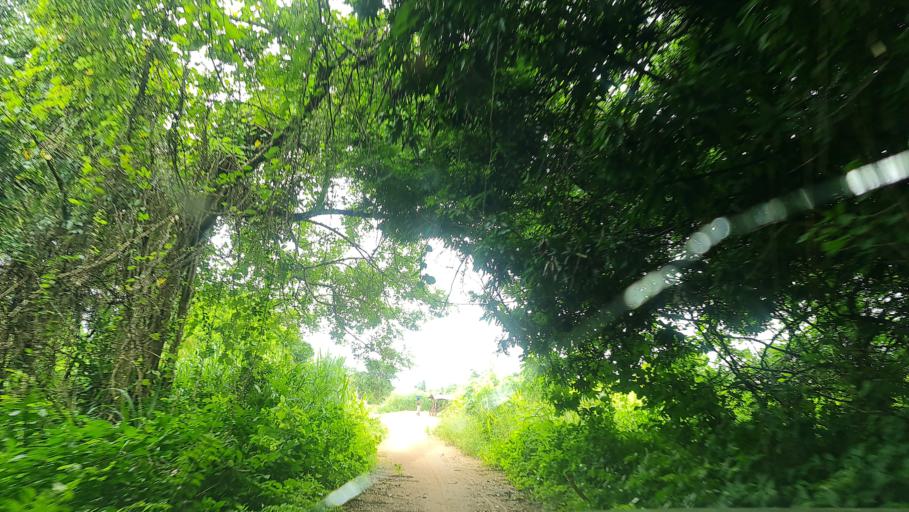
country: MW
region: Southern Region
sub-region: Nsanje District
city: Nsanje
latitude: -17.3870
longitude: 35.7792
